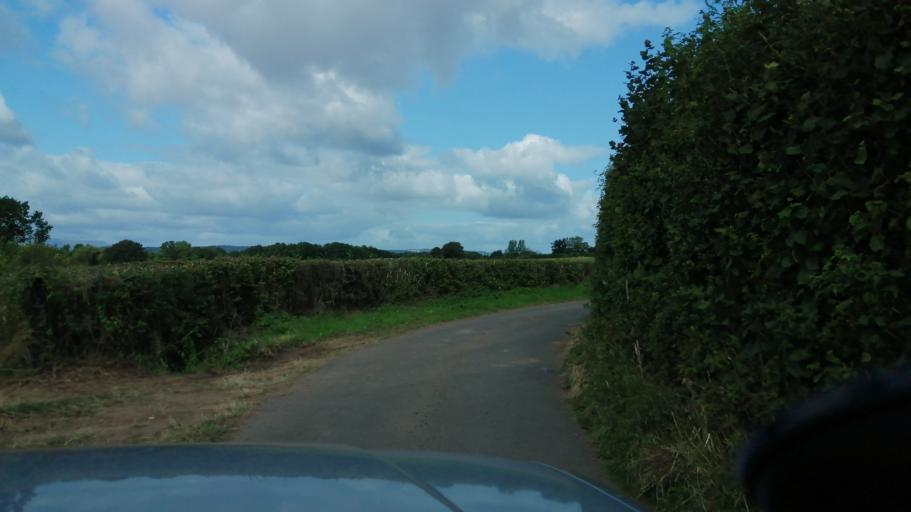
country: GB
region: England
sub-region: Herefordshire
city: Kingstone
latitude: 52.0259
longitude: -2.8088
